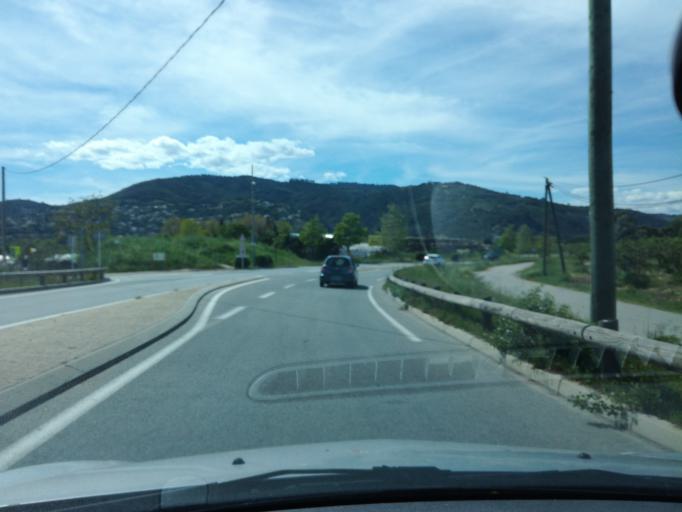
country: FR
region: Provence-Alpes-Cote d'Azur
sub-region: Departement des Alpes-Maritimes
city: Mandelieu-la-Napoule
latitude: 43.5669
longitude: 6.9553
